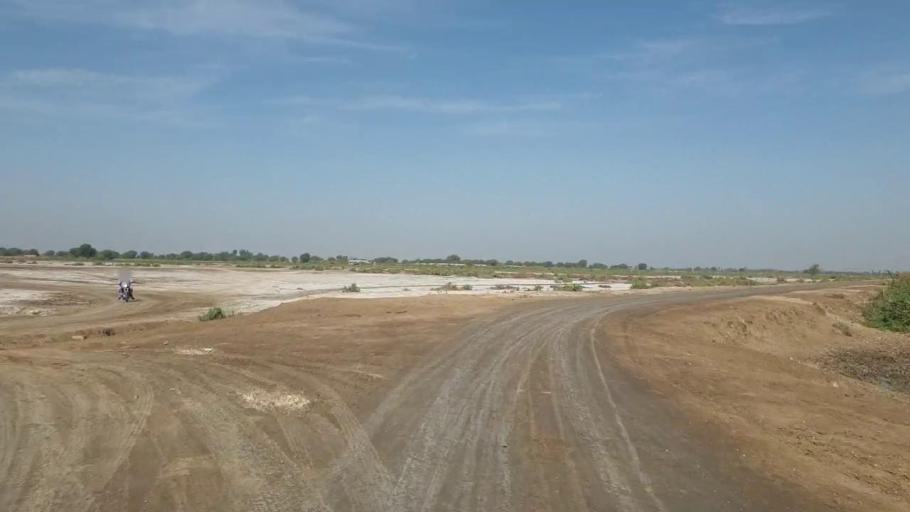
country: PK
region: Sindh
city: Samaro
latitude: 25.3696
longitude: 69.2585
